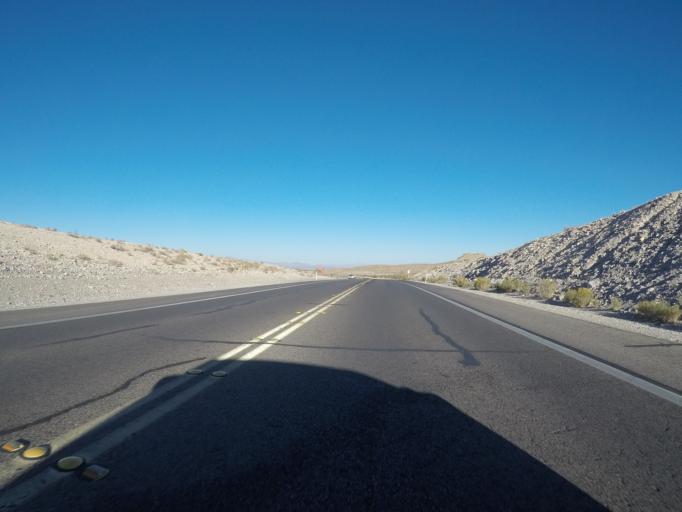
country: US
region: Nevada
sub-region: Clark County
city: Summerlin South
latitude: 36.1485
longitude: -115.3761
